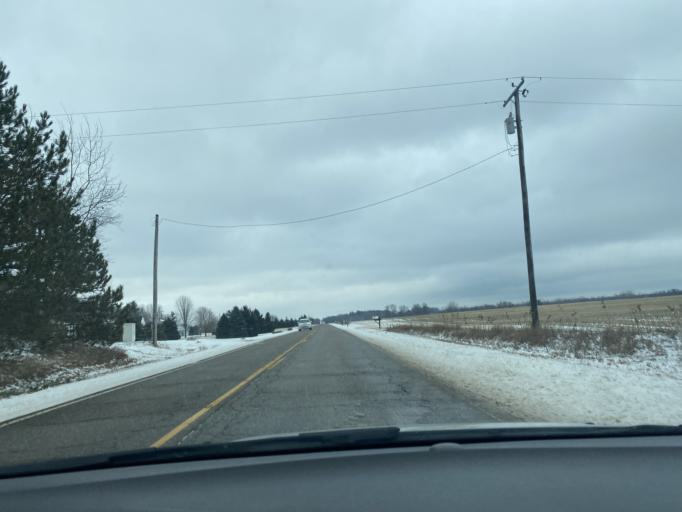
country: US
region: Michigan
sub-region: Lapeer County
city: North Branch
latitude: 43.2065
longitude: -83.2340
